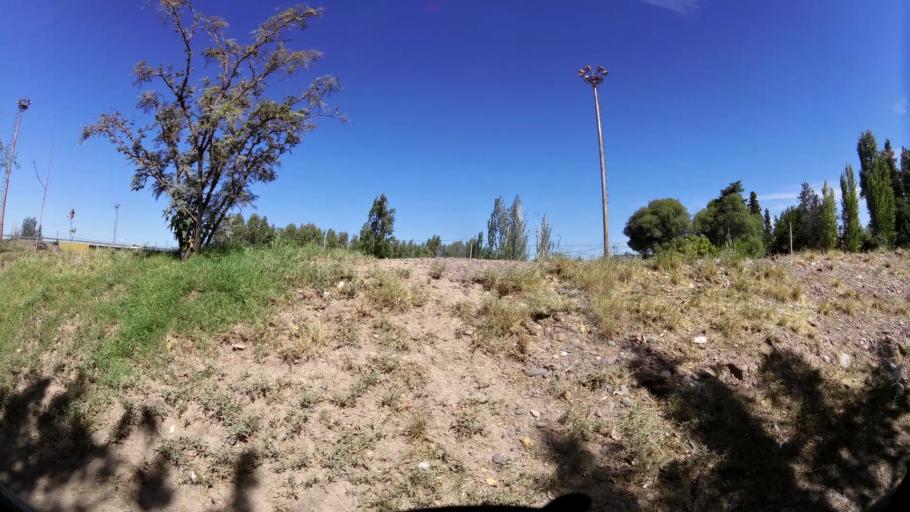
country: AR
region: Mendoza
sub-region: Departamento de Godoy Cruz
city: Godoy Cruz
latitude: -32.9686
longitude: -68.8345
